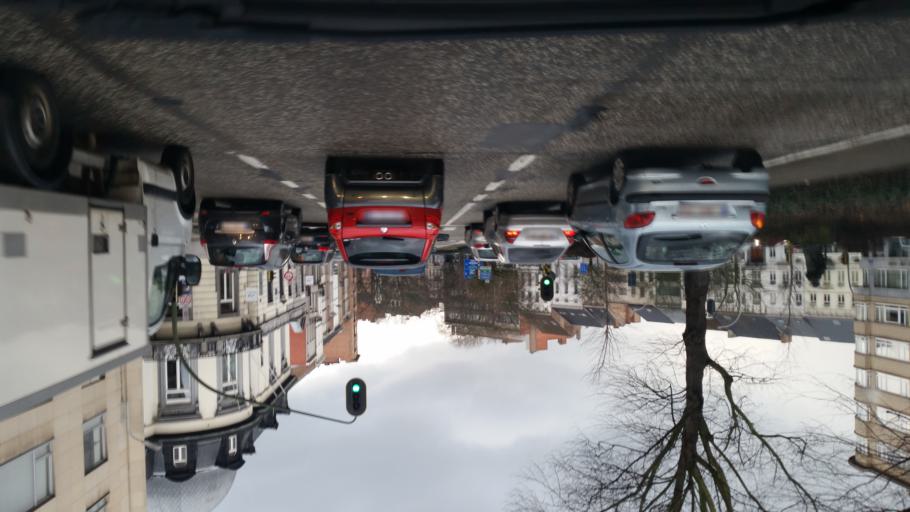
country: BE
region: Flanders
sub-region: Provincie Antwerpen
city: Mechelen
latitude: 51.0210
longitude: 4.4780
